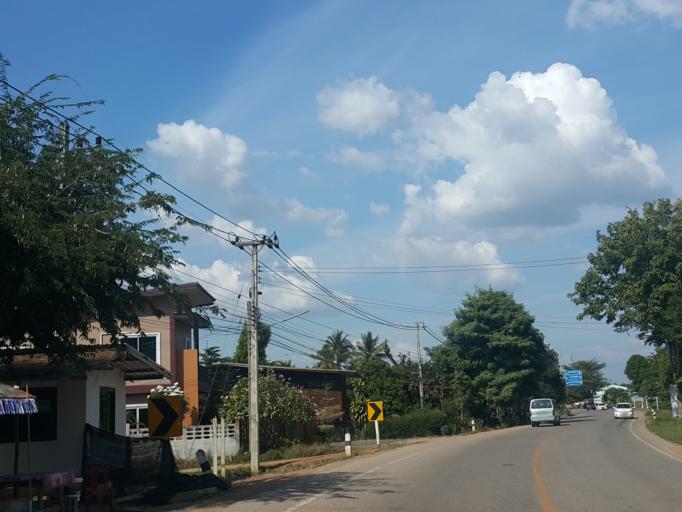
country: TH
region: Sukhothai
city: Sawankhalok
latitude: 17.2971
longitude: 99.8266
